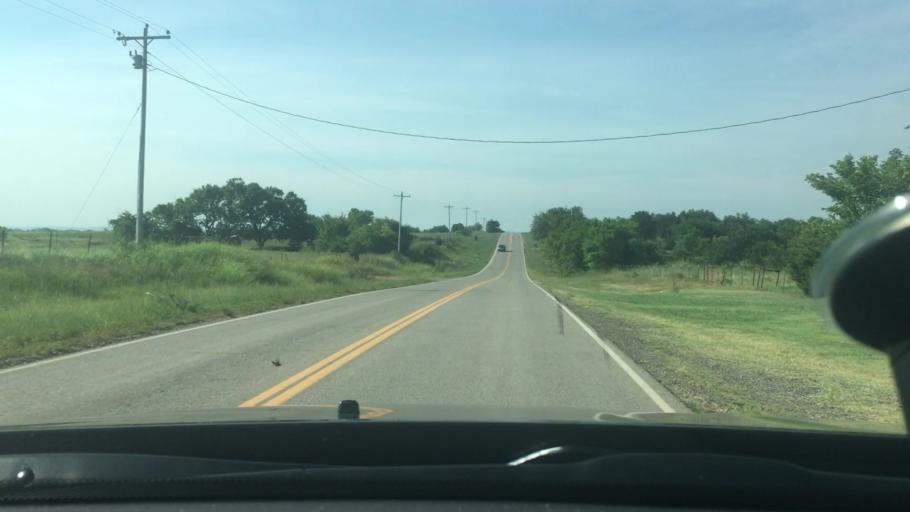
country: US
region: Oklahoma
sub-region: Garvin County
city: Maysville
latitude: 34.6744
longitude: -97.4054
